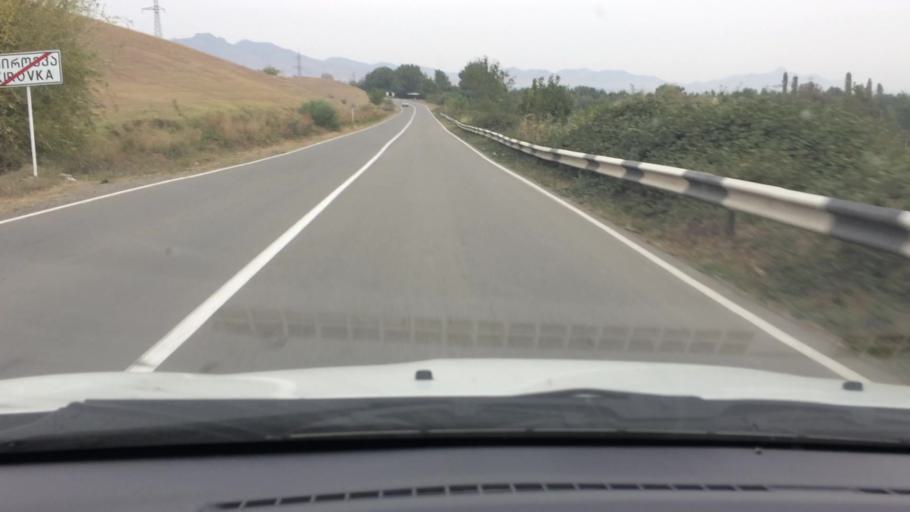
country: AM
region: Tavush
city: Bagratashen
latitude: 41.2824
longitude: 44.7908
